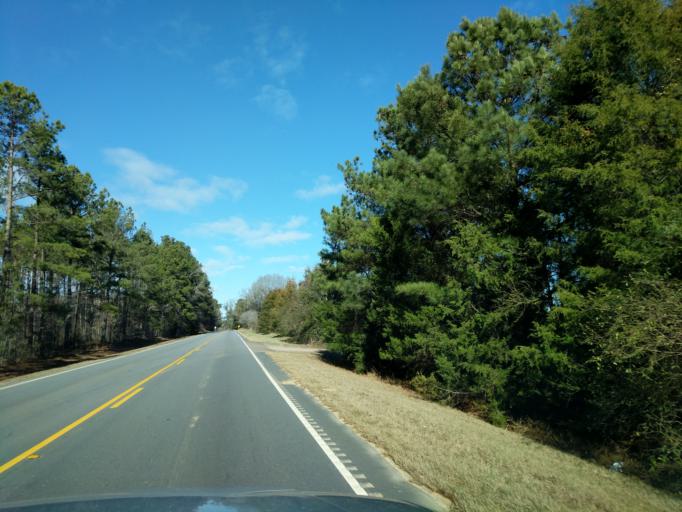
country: US
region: South Carolina
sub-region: Edgefield County
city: Edgefield
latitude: 33.9433
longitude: -82.0479
